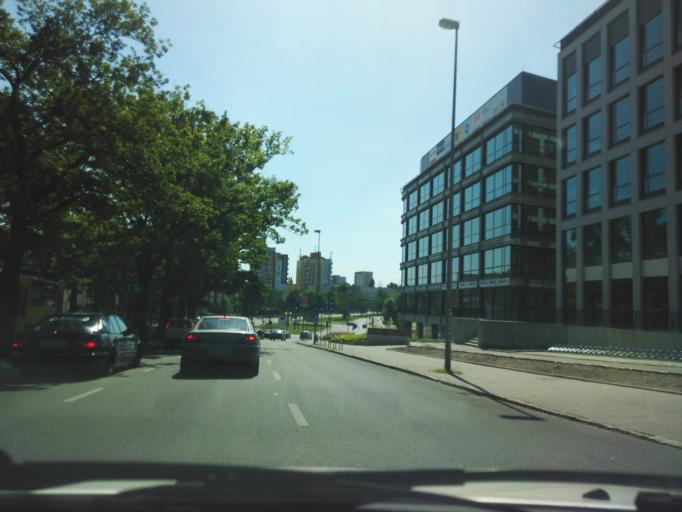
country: PL
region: West Pomeranian Voivodeship
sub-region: Szczecin
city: Szczecin
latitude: 53.4183
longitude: 14.5328
